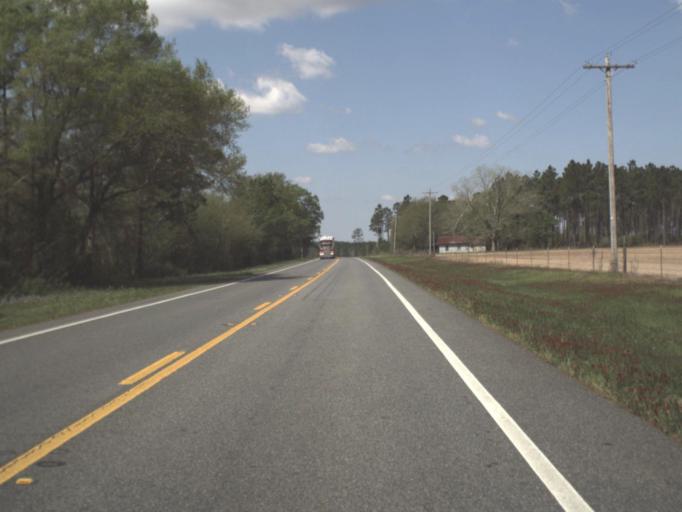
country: US
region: Alabama
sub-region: Escambia County
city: East Brewton
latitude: 30.9507
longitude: -87.0833
